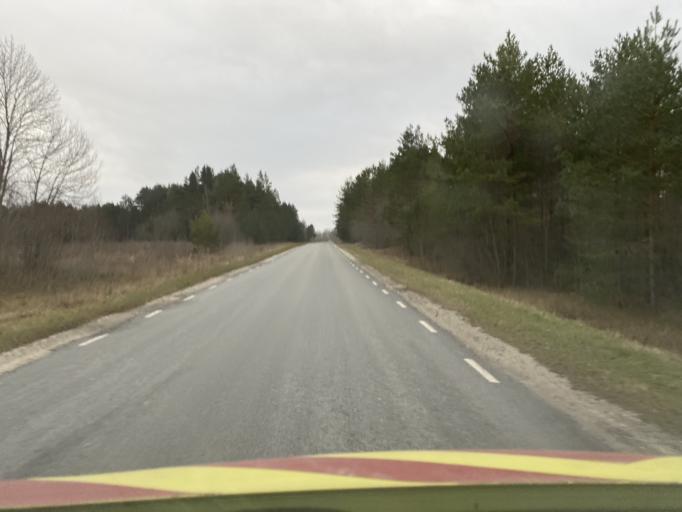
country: EE
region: Laeaene
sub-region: Ridala Parish
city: Uuemoisa
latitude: 59.0355
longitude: 23.6374
